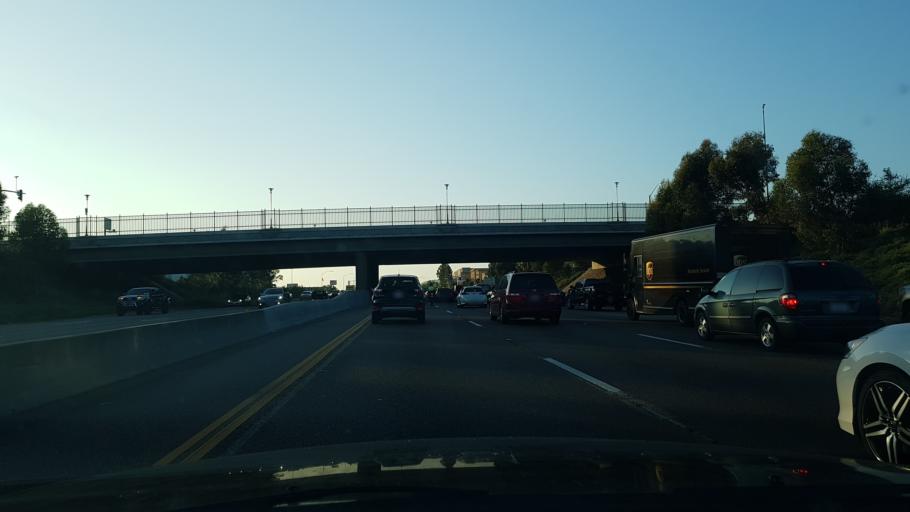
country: US
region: California
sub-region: San Diego County
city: Escondido
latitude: 33.1318
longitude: -117.1204
